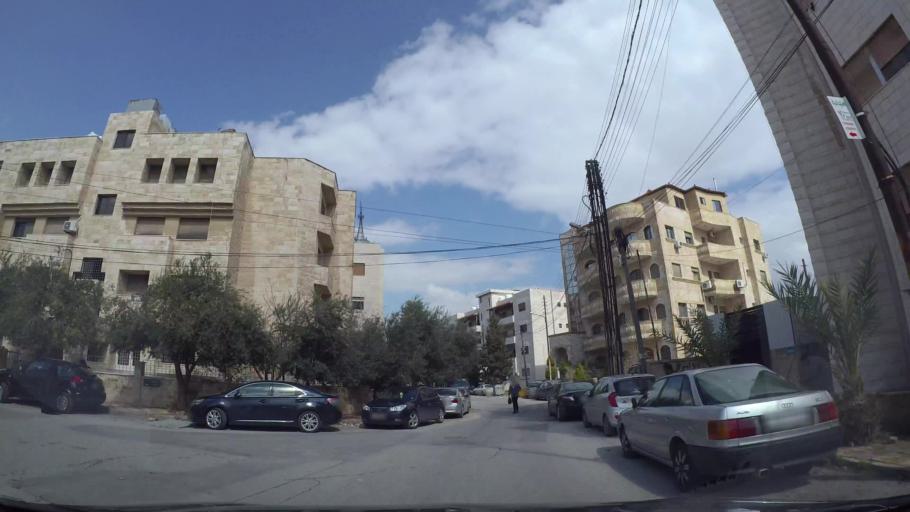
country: JO
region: Amman
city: Amman
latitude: 31.9794
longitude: 35.8984
